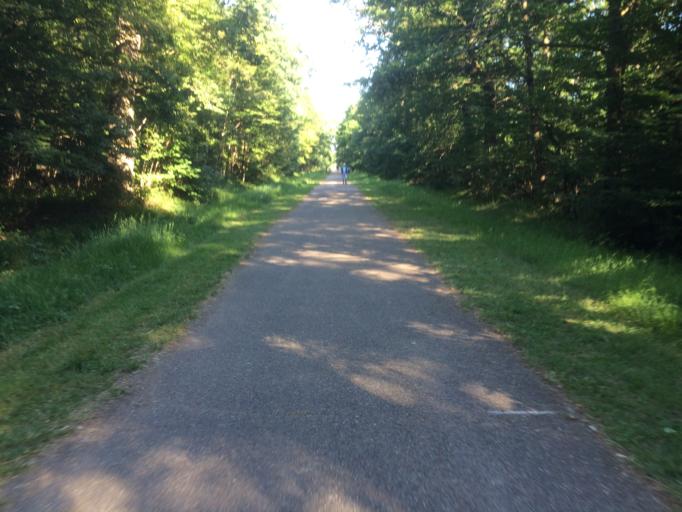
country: FR
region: Ile-de-France
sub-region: Departement du Val-de-Marne
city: Boissy-Saint-Leger
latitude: 48.7457
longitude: 2.5178
